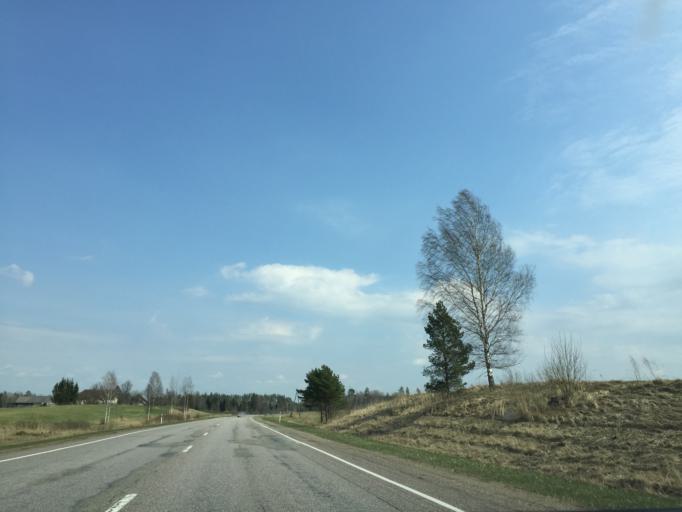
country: LV
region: Apes Novads
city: Ape
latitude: 57.4958
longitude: 26.5846
